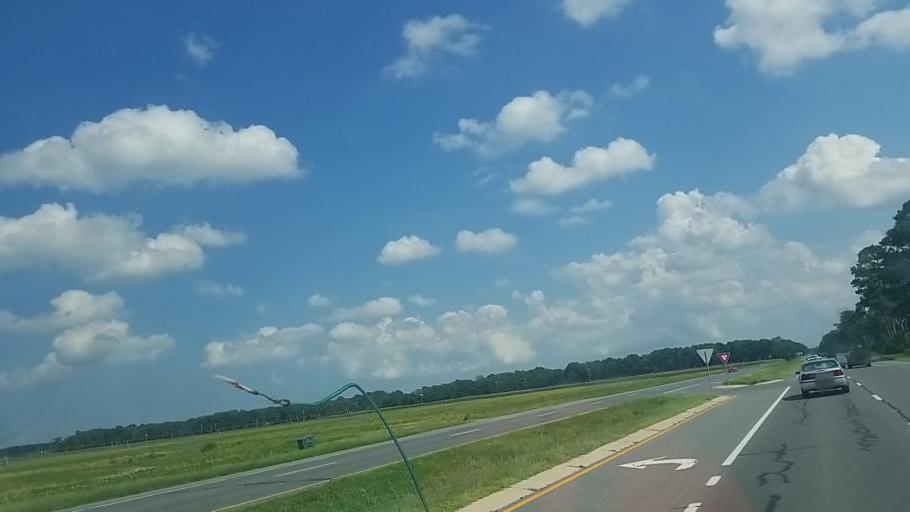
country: US
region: Delaware
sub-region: Sussex County
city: Millsboro
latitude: 38.6210
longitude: -75.3380
